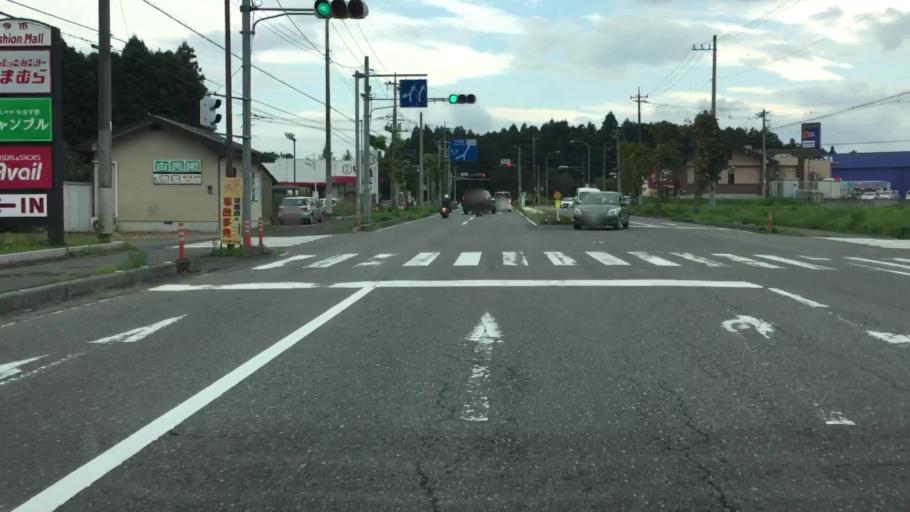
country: JP
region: Tochigi
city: Imaichi
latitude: 36.7435
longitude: 139.7126
